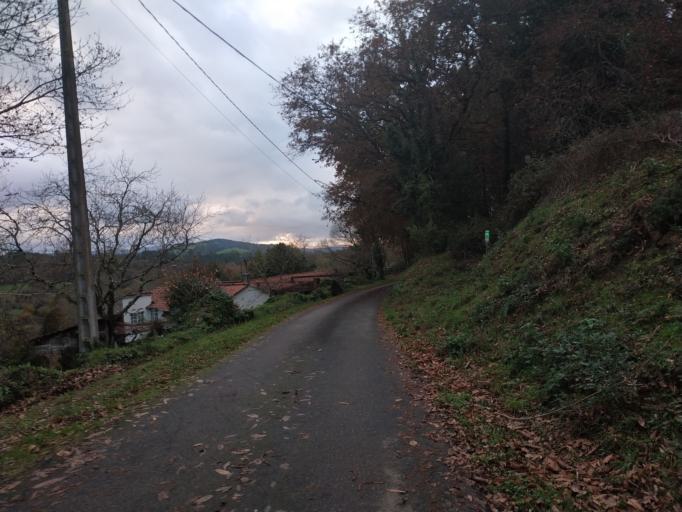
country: ES
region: Galicia
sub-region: Provincia de Pontevedra
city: Silleda
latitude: 42.7833
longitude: -8.1661
